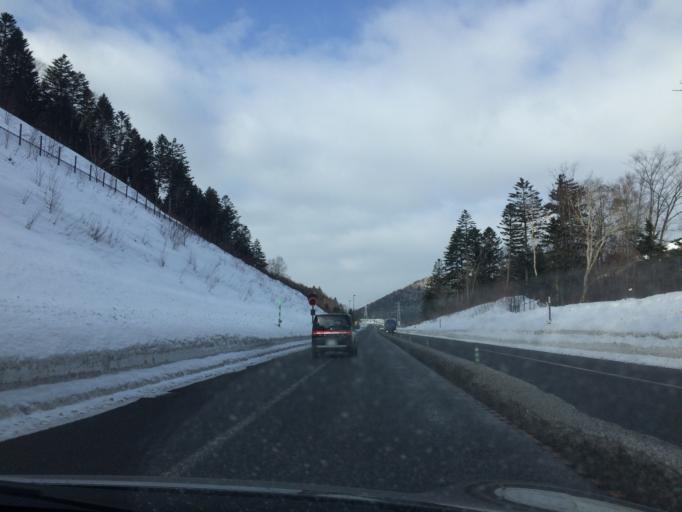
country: JP
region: Hokkaido
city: Shimo-furano
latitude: 43.0528
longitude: 142.6172
